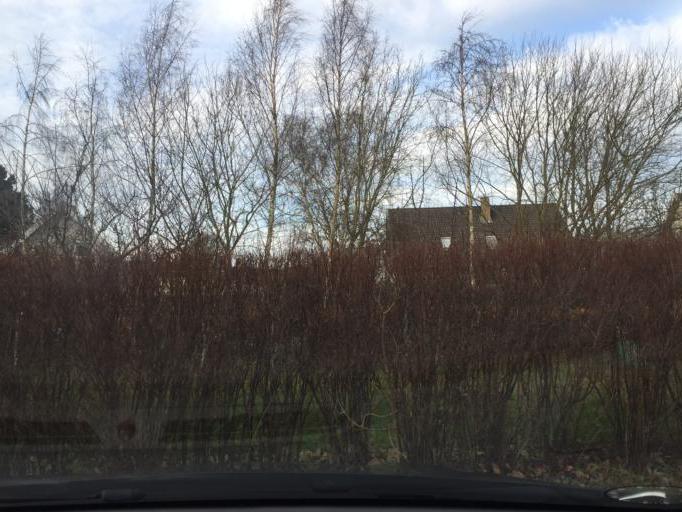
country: DK
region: South Denmark
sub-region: Faaborg-Midtfyn Kommune
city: Ringe
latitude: 55.2033
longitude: 10.4087
